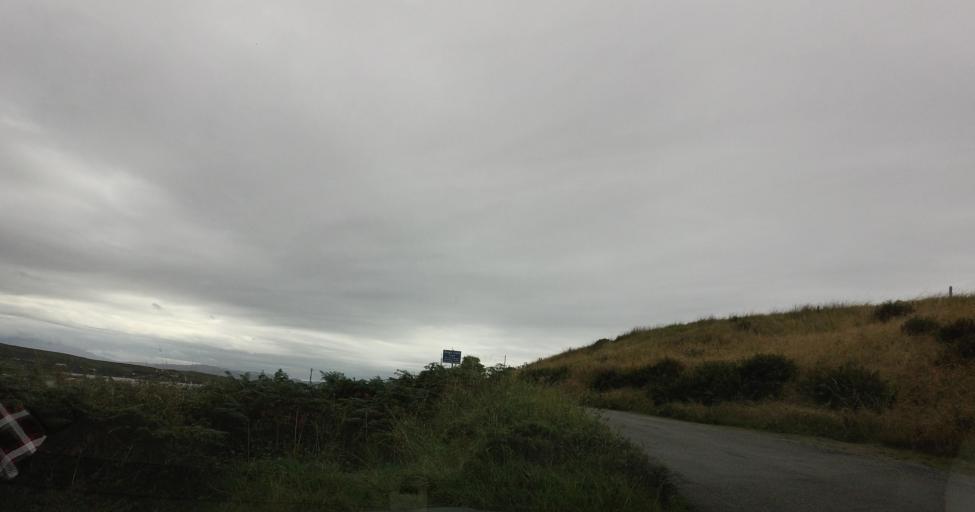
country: GB
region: Scotland
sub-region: Highland
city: Isle of Skye
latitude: 57.4051
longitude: -6.4974
